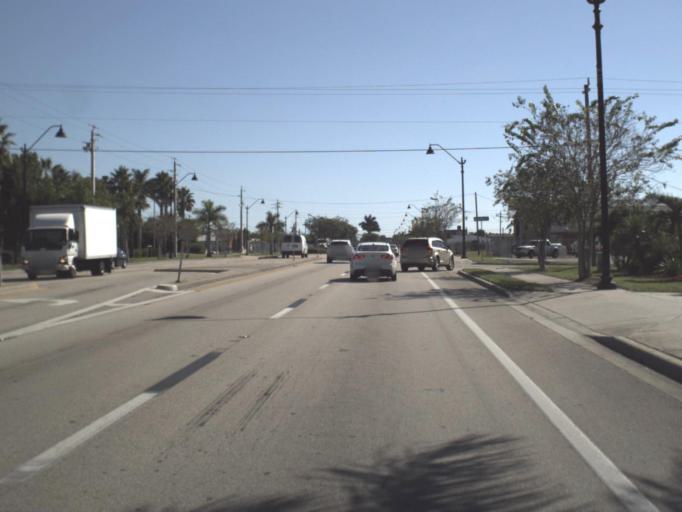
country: US
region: Florida
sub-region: Lee County
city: Fort Myers
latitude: 26.6411
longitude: -81.8387
